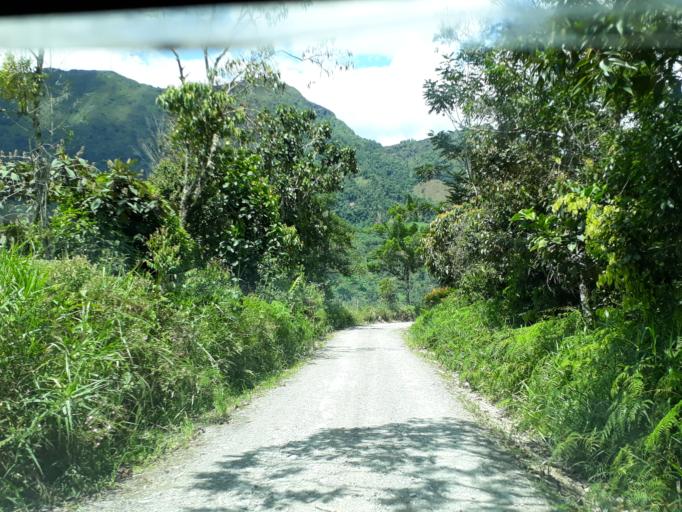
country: CO
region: Cundinamarca
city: Topaipi
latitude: 5.3567
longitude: -74.1959
